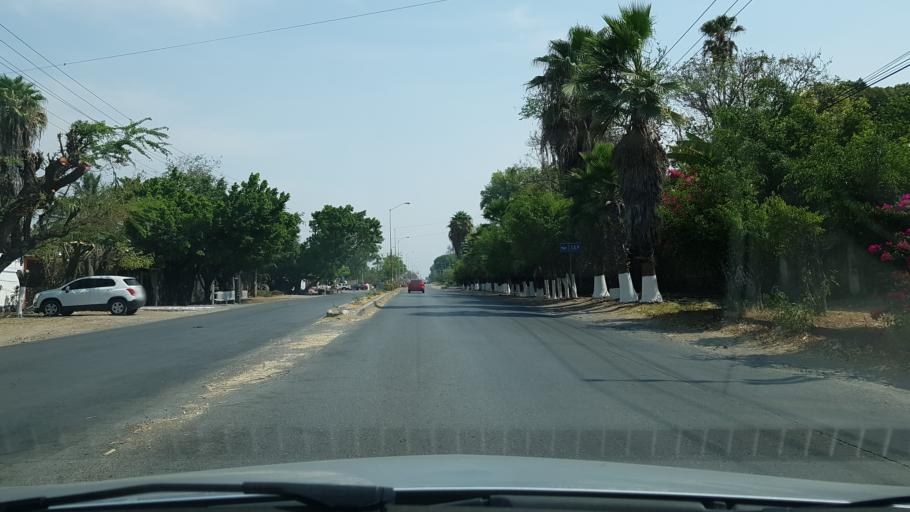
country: MX
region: Morelos
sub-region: Xochitepec
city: Chiconcuac
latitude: 18.7840
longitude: -99.2060
